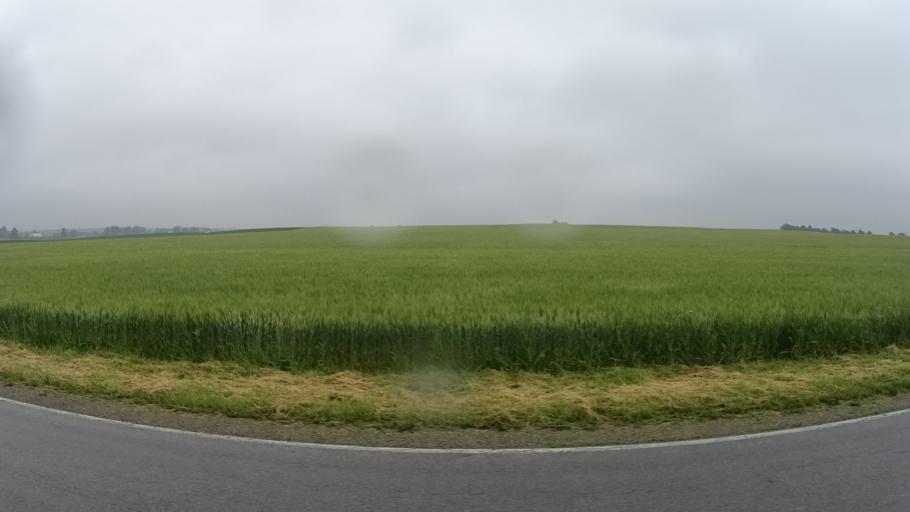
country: US
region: Ohio
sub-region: Huron County
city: Bellevue
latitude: 41.3134
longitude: -82.8425
